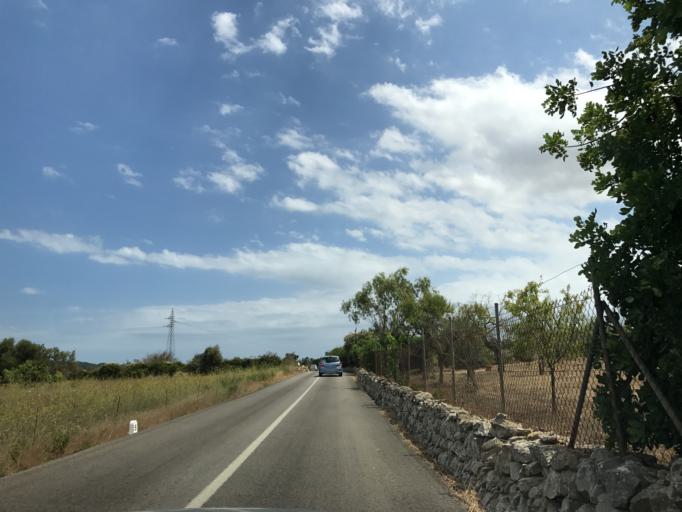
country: ES
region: Balearic Islands
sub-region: Illes Balears
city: Son Servera
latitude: 39.6454
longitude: 3.3461
